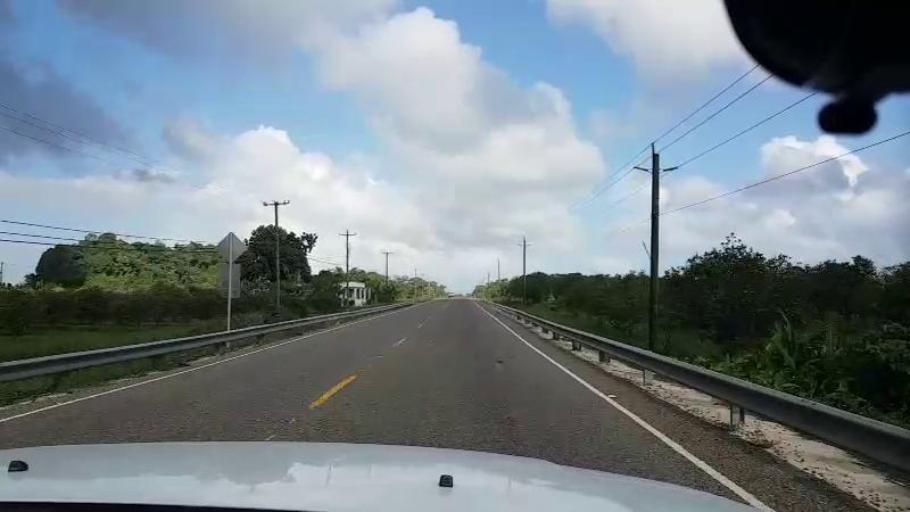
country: BZ
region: Stann Creek
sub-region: Dangriga
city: Dangriga
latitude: 16.9946
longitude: -88.3606
